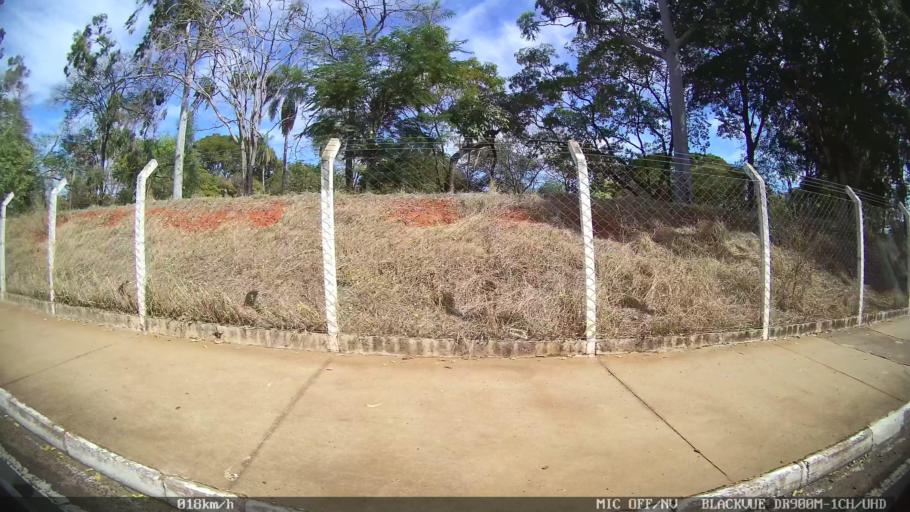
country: BR
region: Sao Paulo
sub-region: Sao Jose Do Rio Preto
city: Sao Jose do Rio Preto
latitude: -20.8204
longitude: -49.3558
